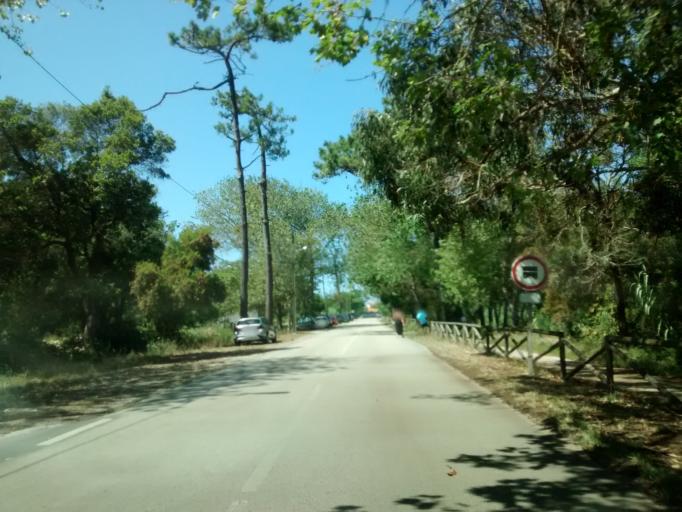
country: PT
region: Coimbra
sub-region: Mira
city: Mira
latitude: 40.4455
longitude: -8.7988
